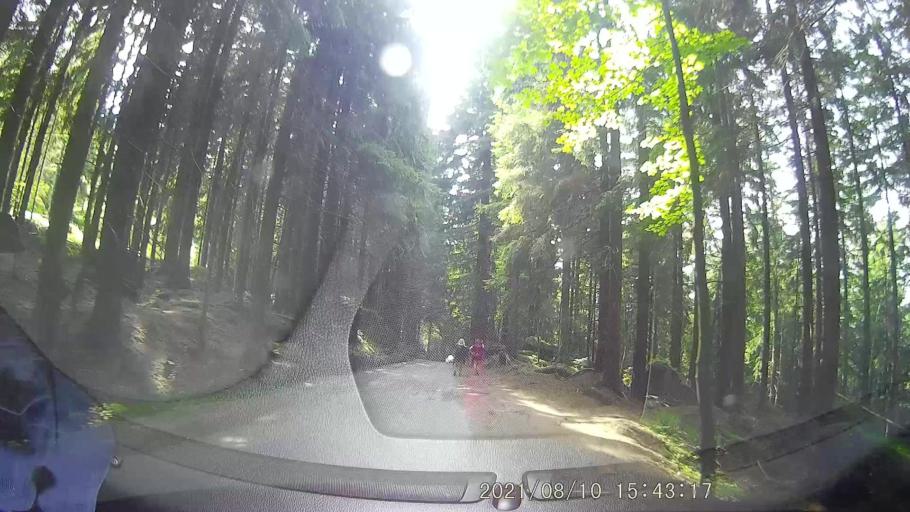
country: CZ
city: Machov
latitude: 50.4869
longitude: 16.3349
